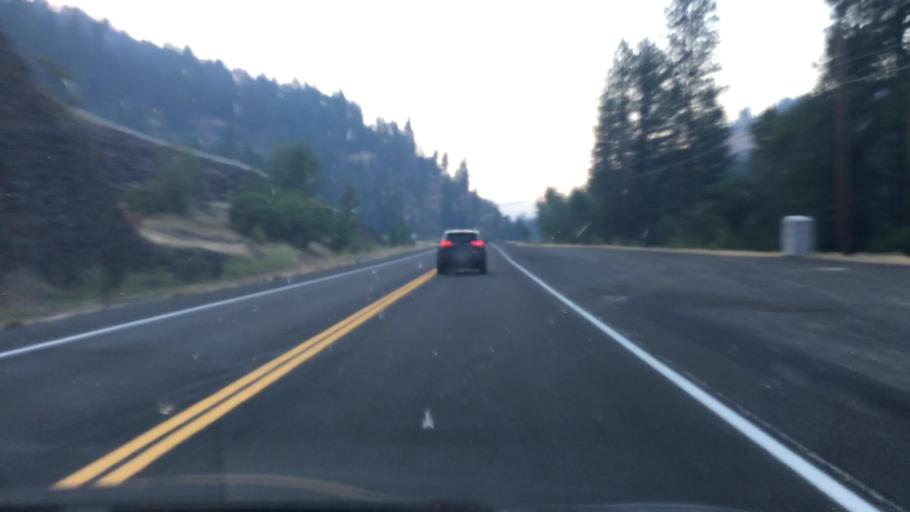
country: US
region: Idaho
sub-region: Valley County
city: McCall
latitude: 45.2154
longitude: -116.3165
